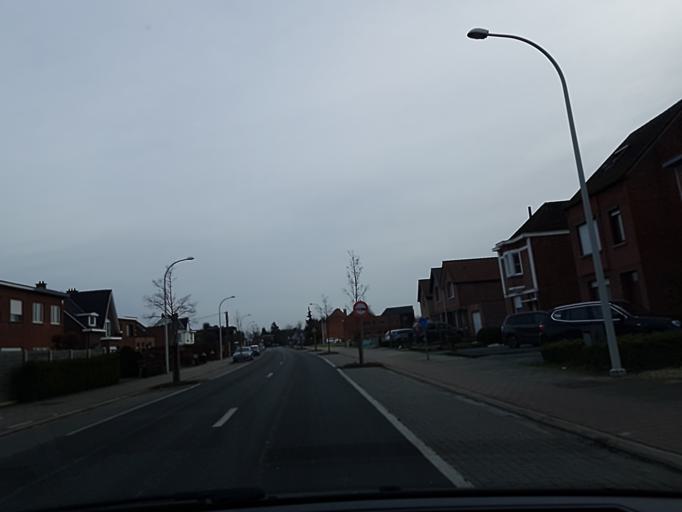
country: BE
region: Flanders
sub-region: Provincie Antwerpen
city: Lier
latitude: 51.1020
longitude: 4.6036
